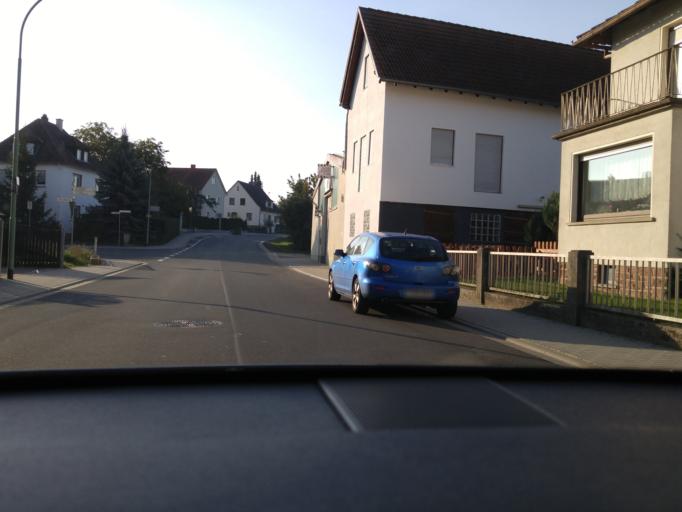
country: DE
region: Hesse
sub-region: Regierungsbezirk Darmstadt
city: Friedberg
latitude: 50.3300
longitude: 8.7183
